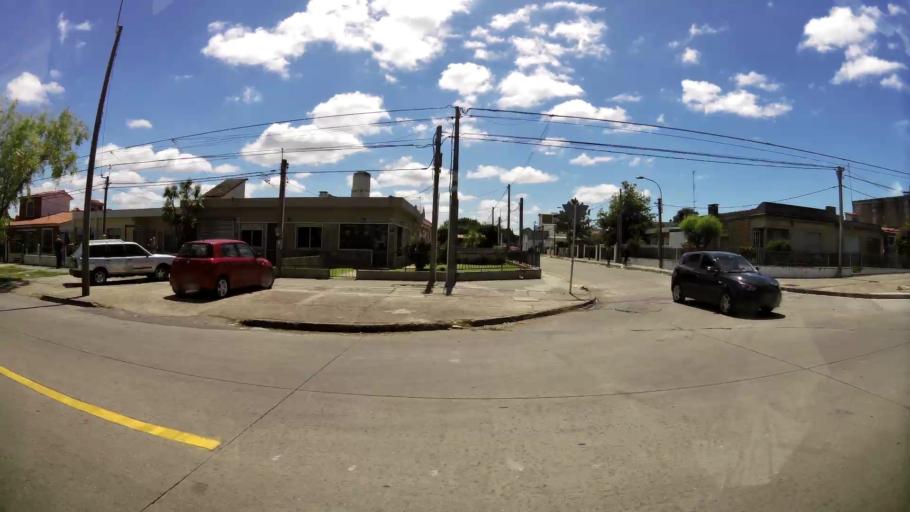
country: UY
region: Canelones
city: Paso de Carrasco
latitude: -34.8690
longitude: -56.1187
